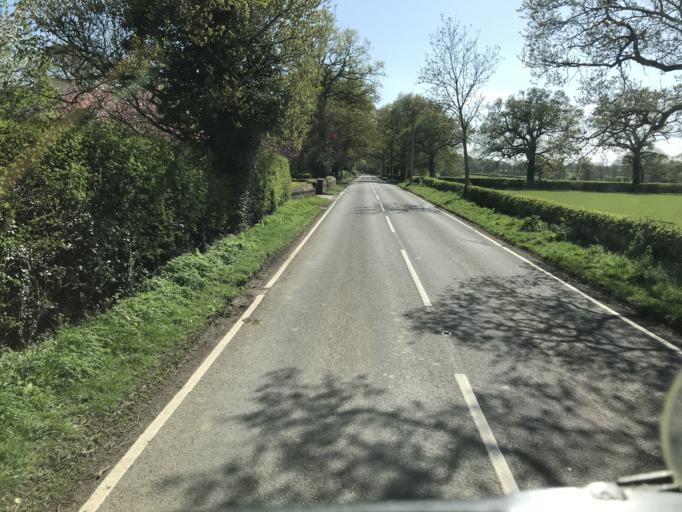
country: GB
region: England
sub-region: Cheshire East
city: Nantwich
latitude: 53.1020
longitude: -2.5121
